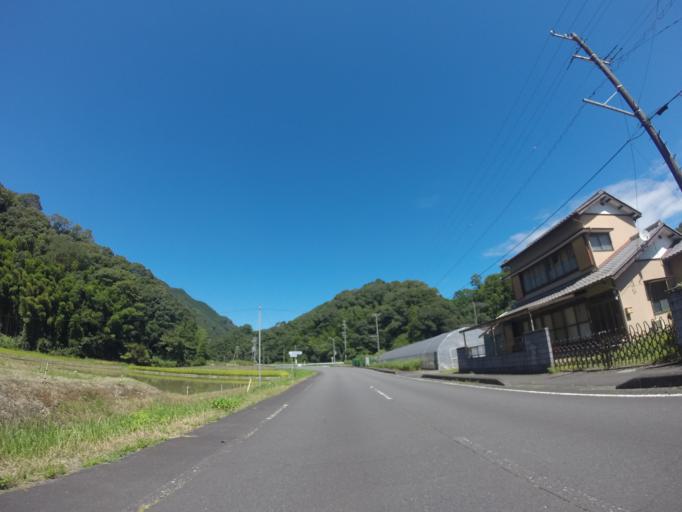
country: JP
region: Shizuoka
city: Fujieda
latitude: 34.9130
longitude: 138.1913
